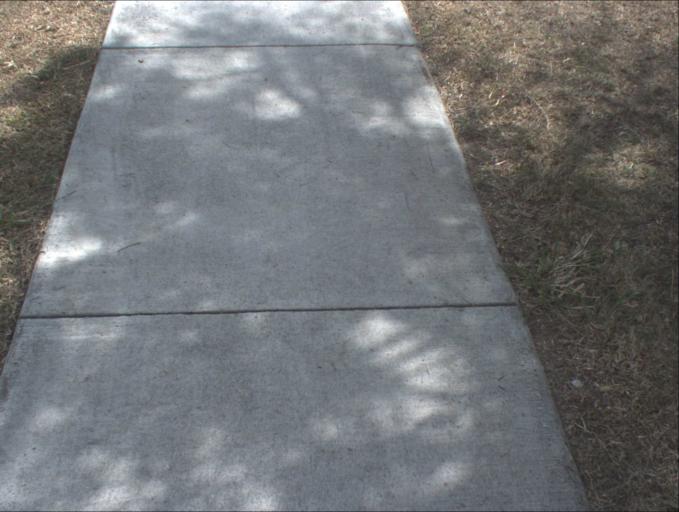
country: AU
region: Queensland
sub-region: Logan
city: Beenleigh
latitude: -27.7187
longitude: 153.1908
